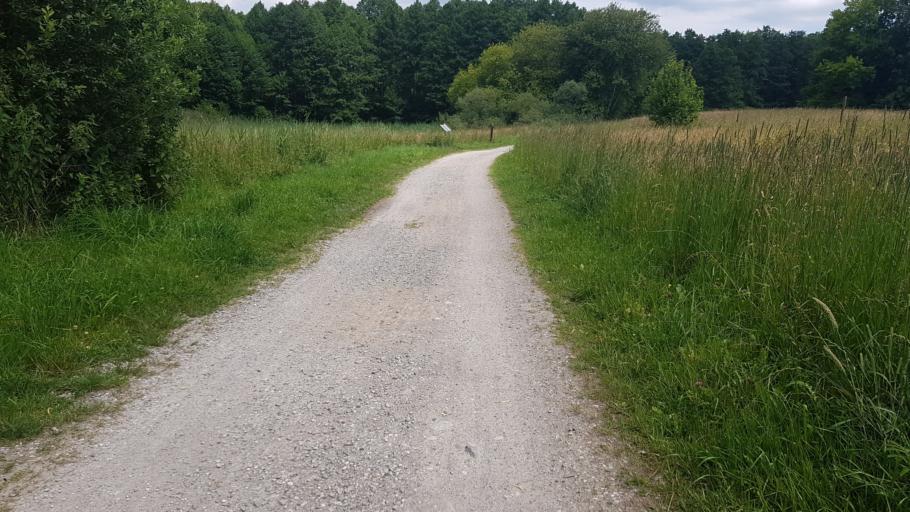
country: DE
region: Bavaria
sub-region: Upper Bavaria
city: Starnberg
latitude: 48.0058
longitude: 11.3662
